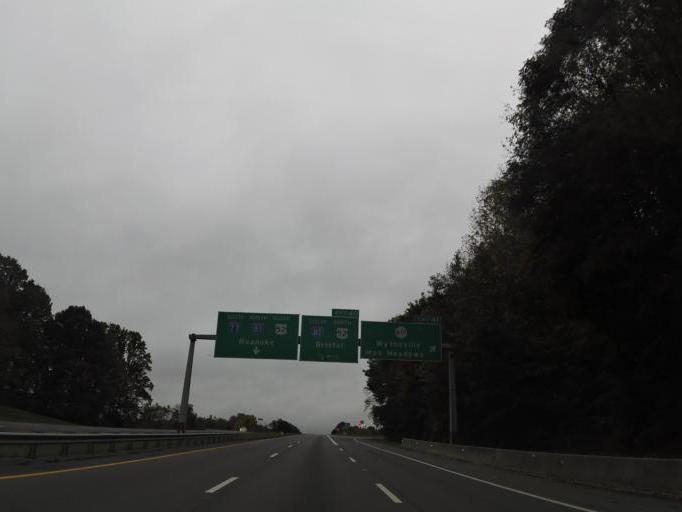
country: US
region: Virginia
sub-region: Wythe County
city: Wytheville
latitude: 36.9727
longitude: -81.0677
